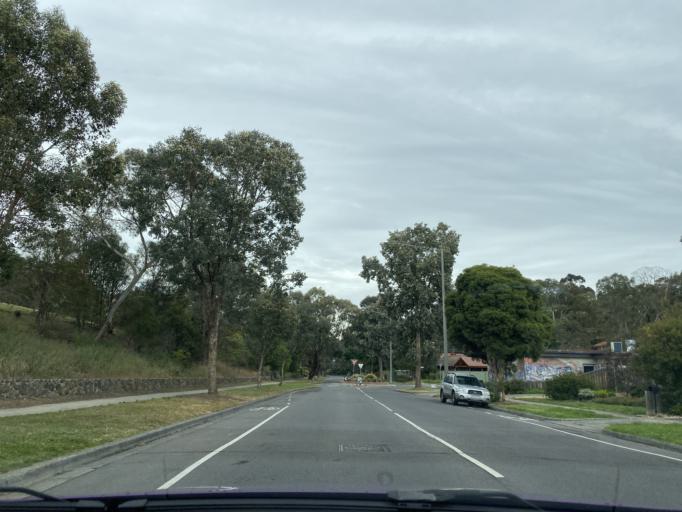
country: AU
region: Victoria
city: Saint Helena
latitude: -37.6988
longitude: 145.1318
